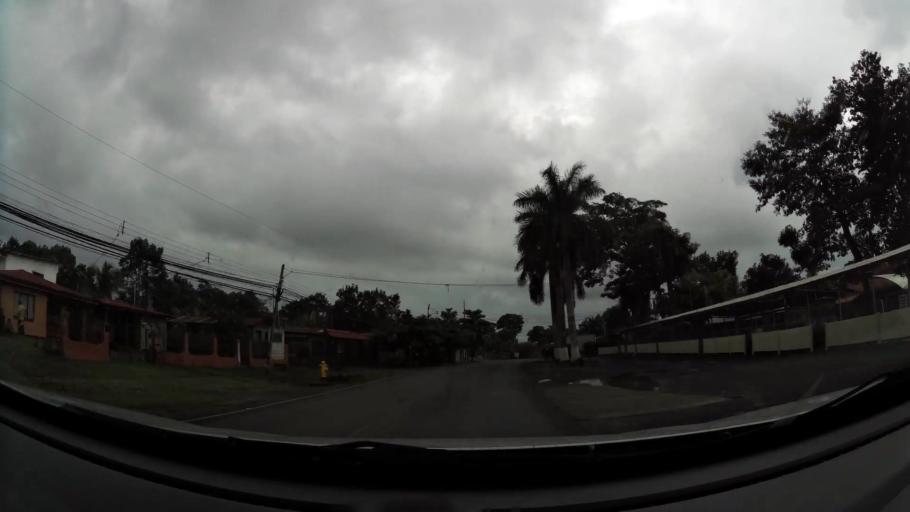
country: CR
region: Puntarenas
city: Esparza
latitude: 9.9952
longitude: -84.6443
